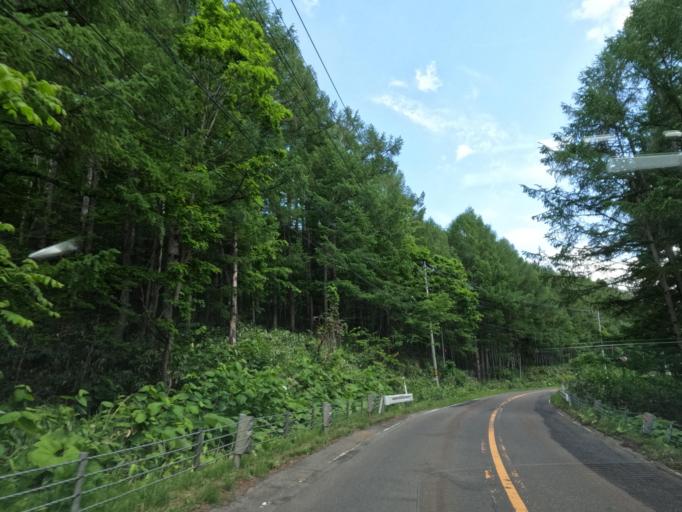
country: JP
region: Hokkaido
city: Takikawa
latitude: 43.5781
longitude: 141.8338
